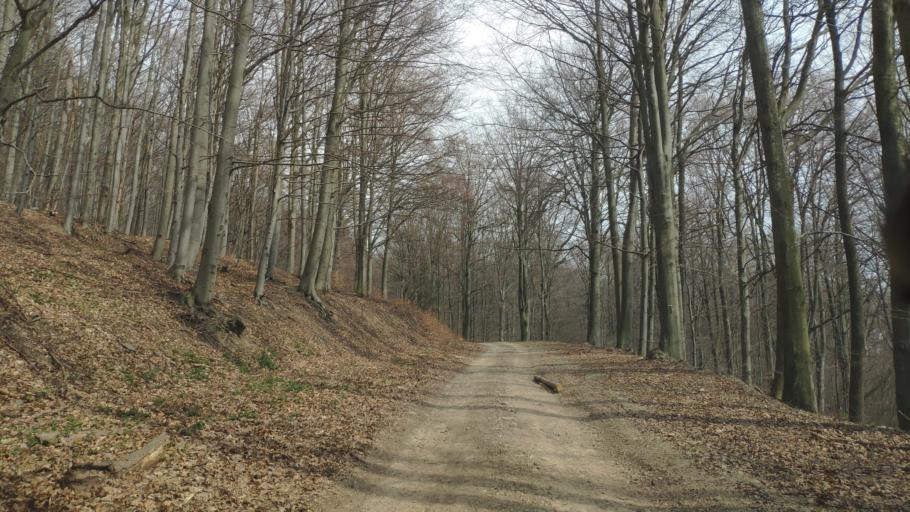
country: SK
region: Kosicky
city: Moldava nad Bodvou
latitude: 48.7424
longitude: 21.0395
